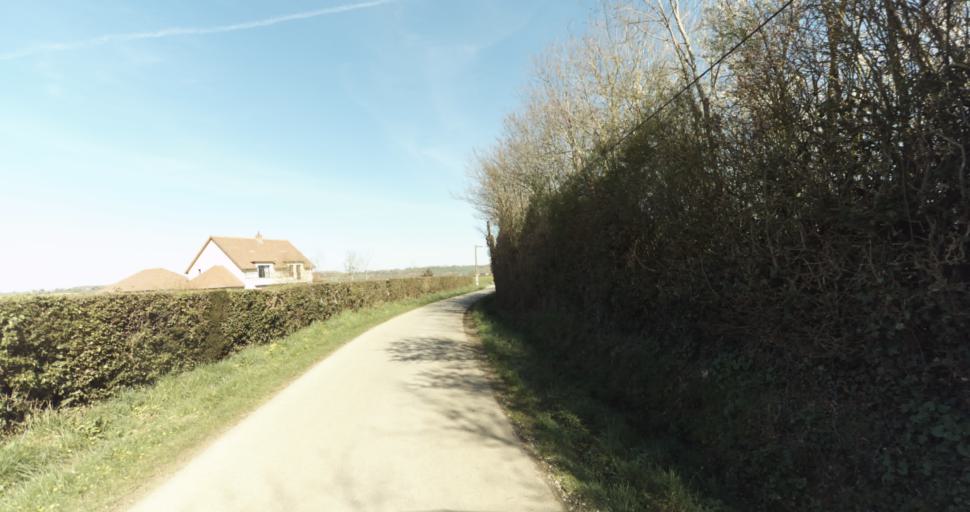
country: FR
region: Lower Normandy
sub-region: Departement du Calvados
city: Saint-Pierre-sur-Dives
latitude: 49.0366
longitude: -0.0043
